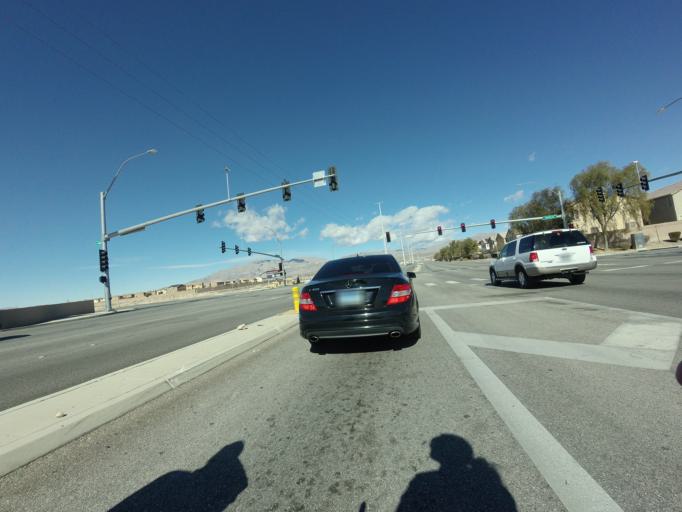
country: US
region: Nevada
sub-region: Clark County
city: Nellis Air Force Base
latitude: 36.2690
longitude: -115.0800
